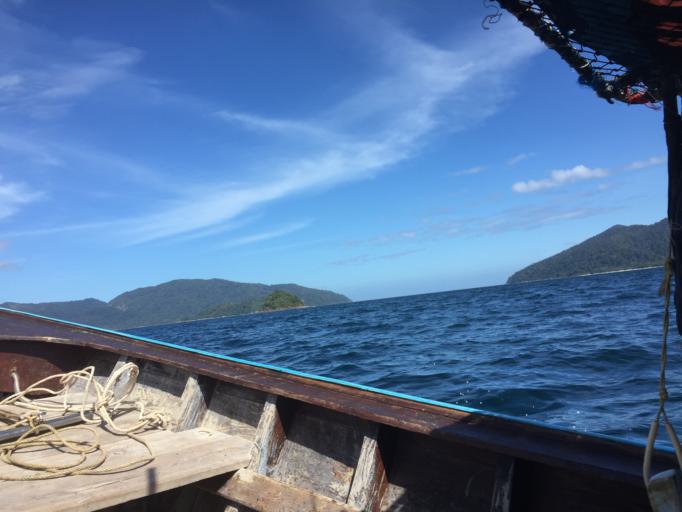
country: MY
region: Kedah
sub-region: Langkawi
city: Kuah
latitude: 6.5102
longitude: 99.2777
